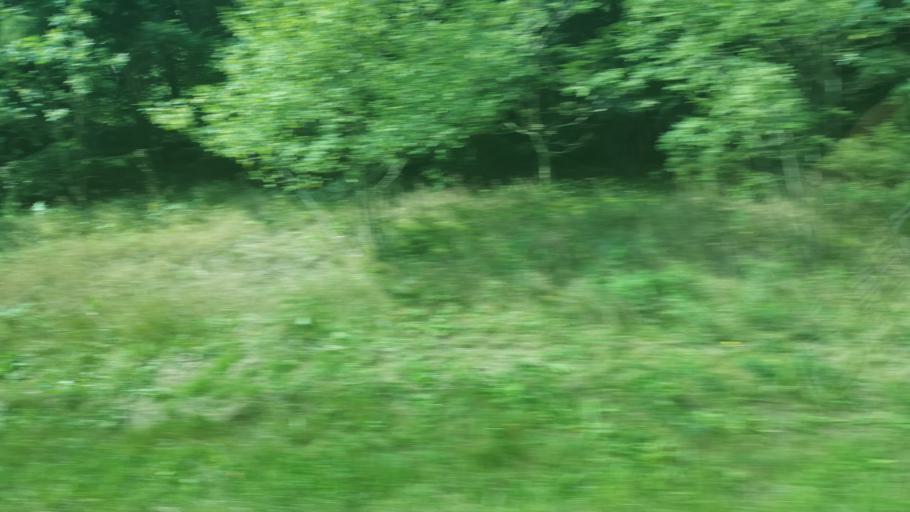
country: DE
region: Bavaria
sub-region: Upper Palatinate
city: Pemfling
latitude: 49.2751
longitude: 12.6292
